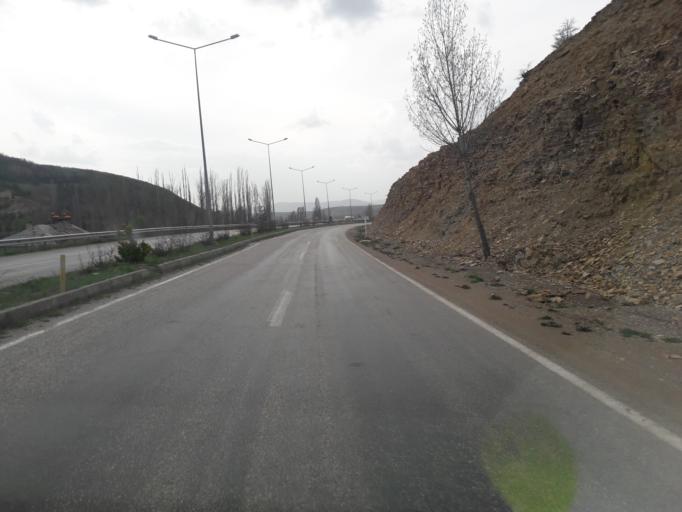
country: TR
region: Gumushane
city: Siran
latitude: 40.1767
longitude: 39.1307
